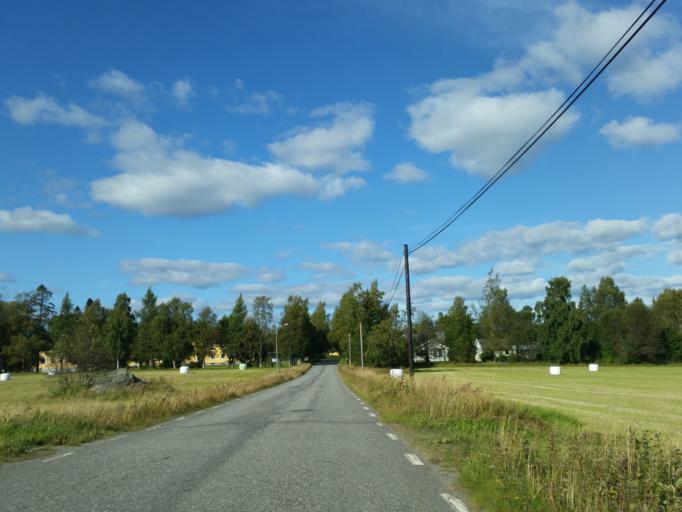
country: SE
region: Vaesterbotten
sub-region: Robertsfors Kommun
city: Robertsfors
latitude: 64.0423
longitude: 20.8581
